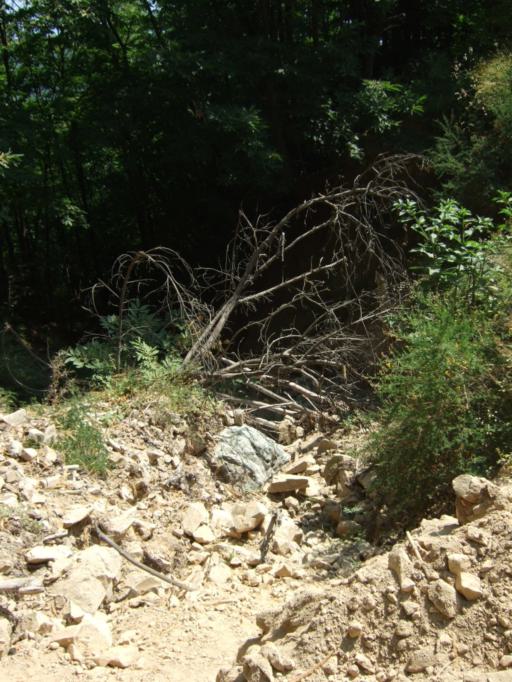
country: GR
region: Mount Athos
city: Karyes
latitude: 40.1932
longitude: 24.2958
